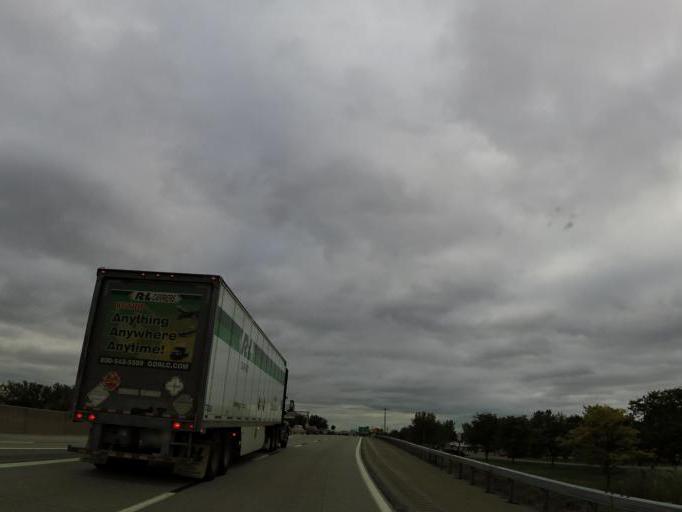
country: US
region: New York
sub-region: Erie County
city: Sloan
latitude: 42.8732
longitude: -78.7897
